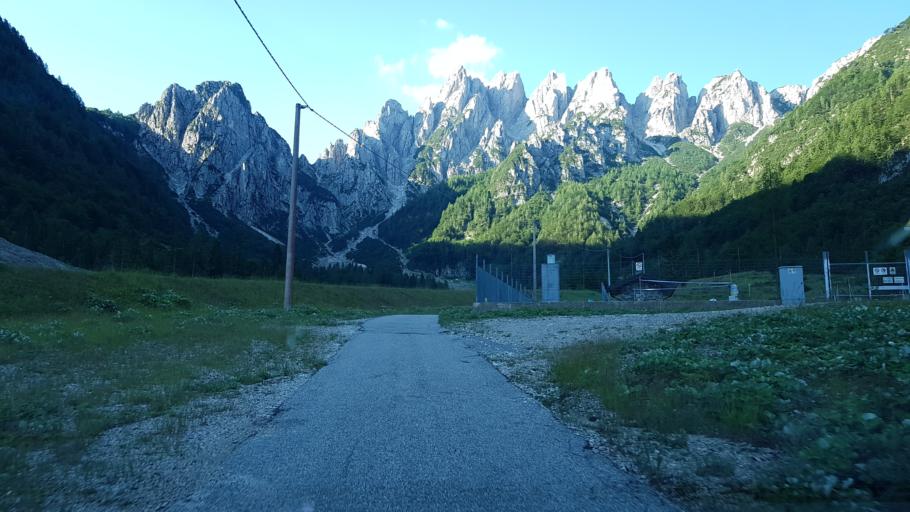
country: IT
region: Friuli Venezia Giulia
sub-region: Provincia di Udine
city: Pontebba
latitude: 46.4901
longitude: 13.2550
